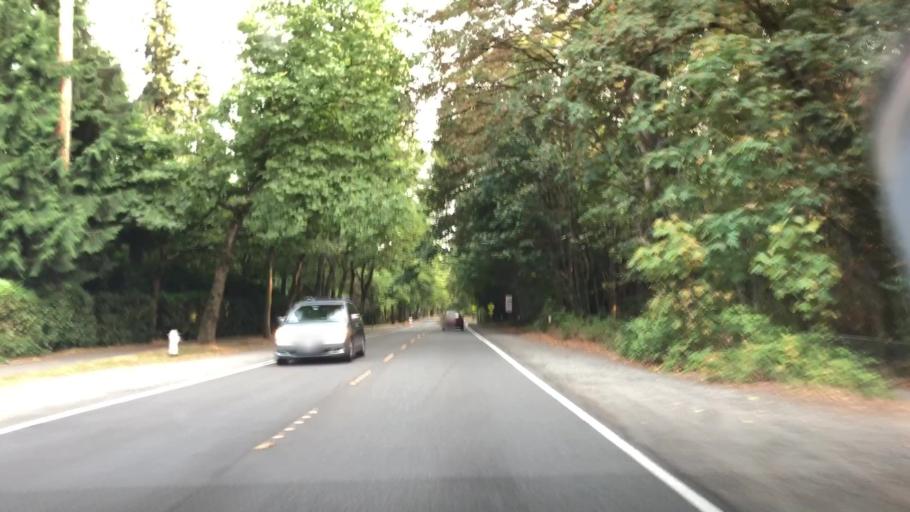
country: US
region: Washington
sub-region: King County
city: Mercer Island
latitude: 47.5529
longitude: -122.2216
